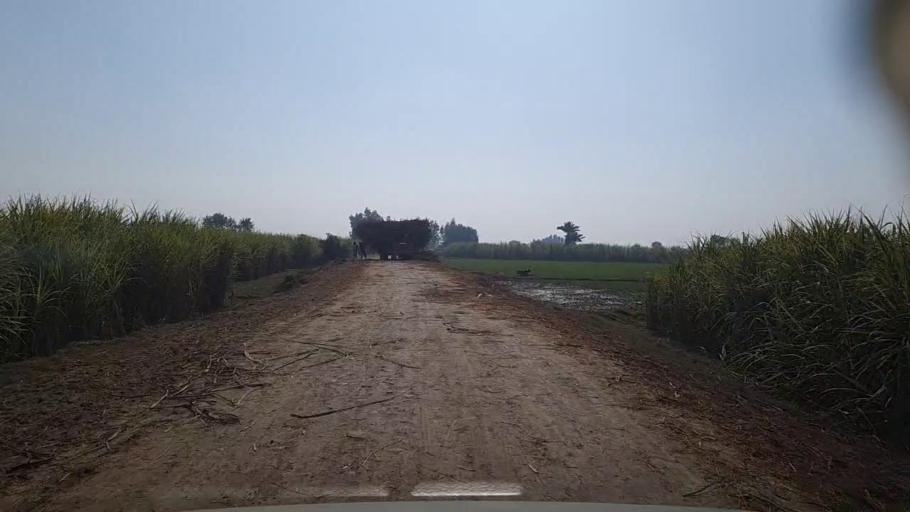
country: PK
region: Sindh
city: Mirpur Mathelo
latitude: 28.0685
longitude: 69.6172
